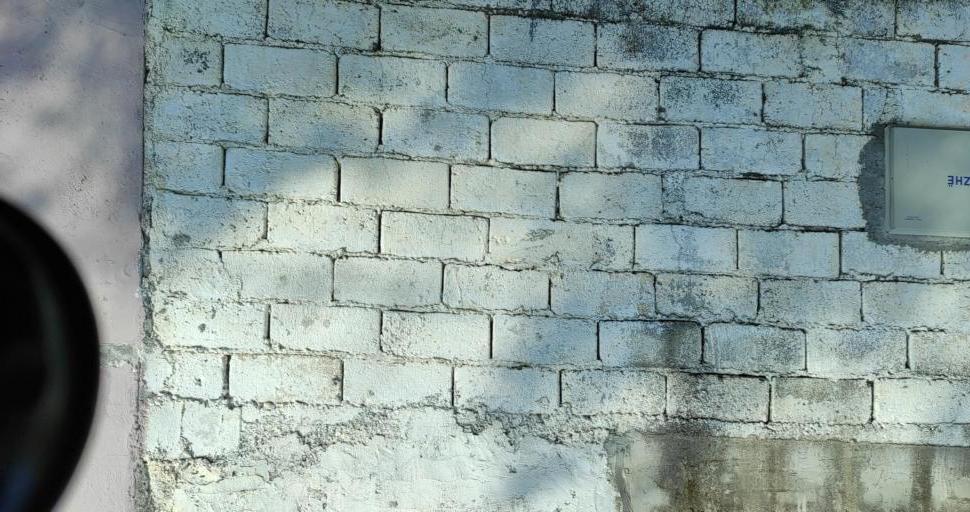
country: AL
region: Lezhe
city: Lezhe
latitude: 41.7875
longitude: 19.6457
